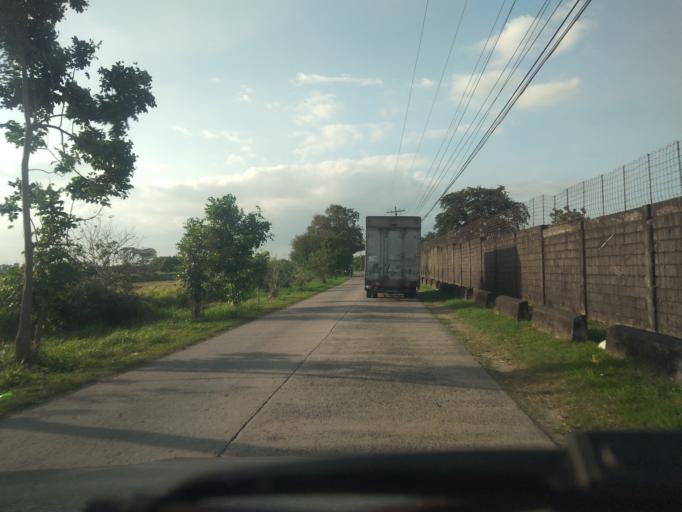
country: PH
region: Central Luzon
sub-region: Province of Pampanga
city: Malino
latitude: 15.1094
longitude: 120.6687
